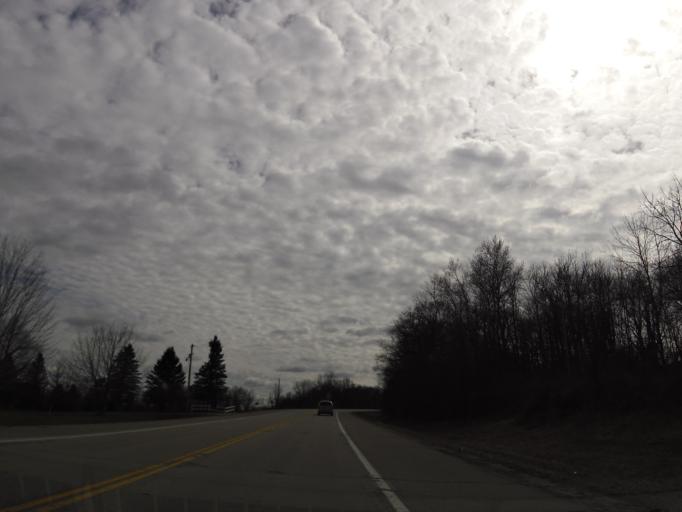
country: US
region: Minnesota
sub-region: Olmsted County
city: Stewartville
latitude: 43.8887
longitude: -92.4073
